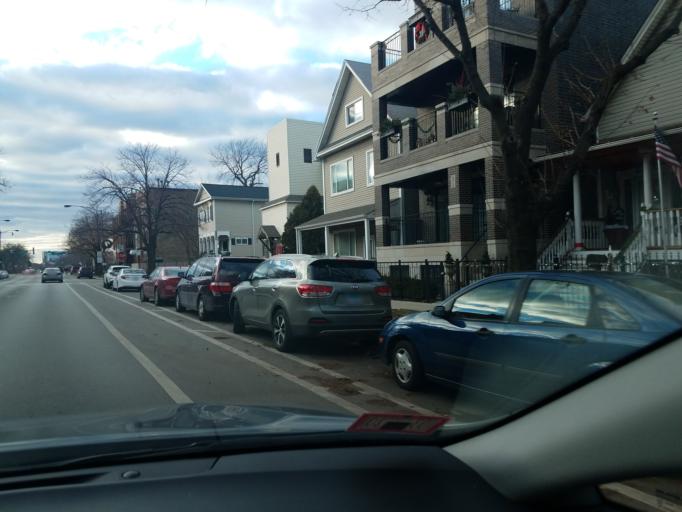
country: US
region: Illinois
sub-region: Cook County
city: Lincolnwood
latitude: 41.9432
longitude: -87.6862
